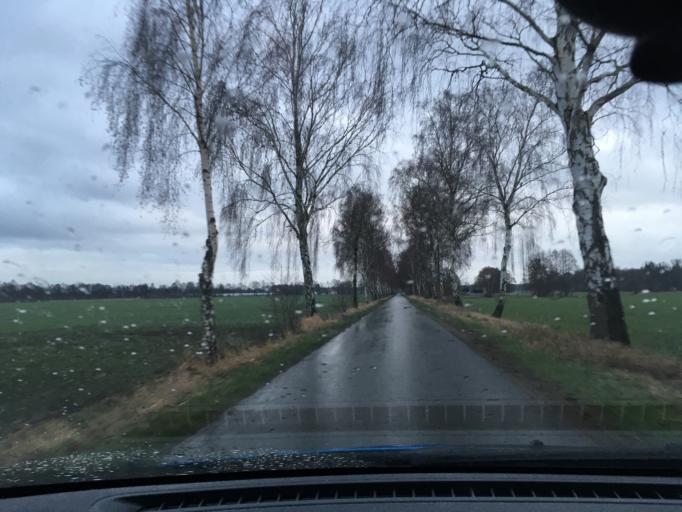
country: DE
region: Lower Saxony
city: Ludersburg
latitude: 53.3178
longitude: 10.6019
